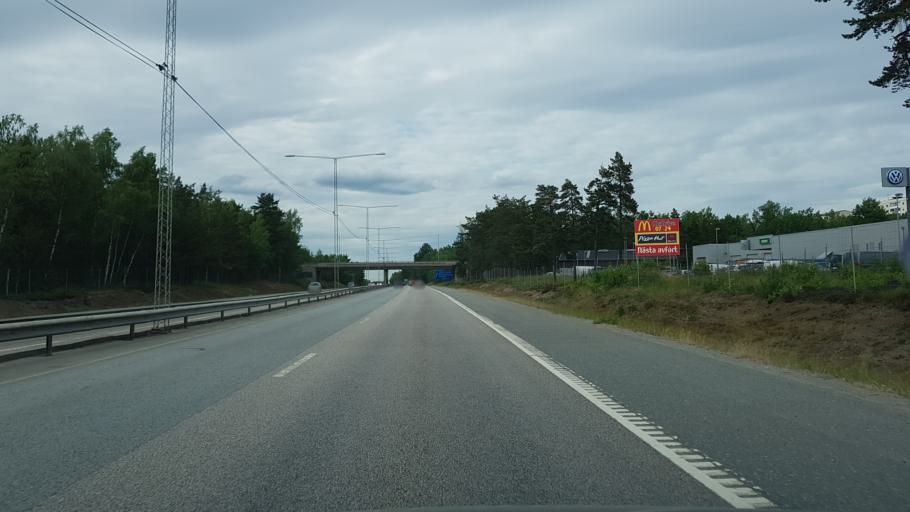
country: SE
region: Stockholm
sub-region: Haninge Kommun
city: Haninge
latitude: 59.1658
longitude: 18.1592
